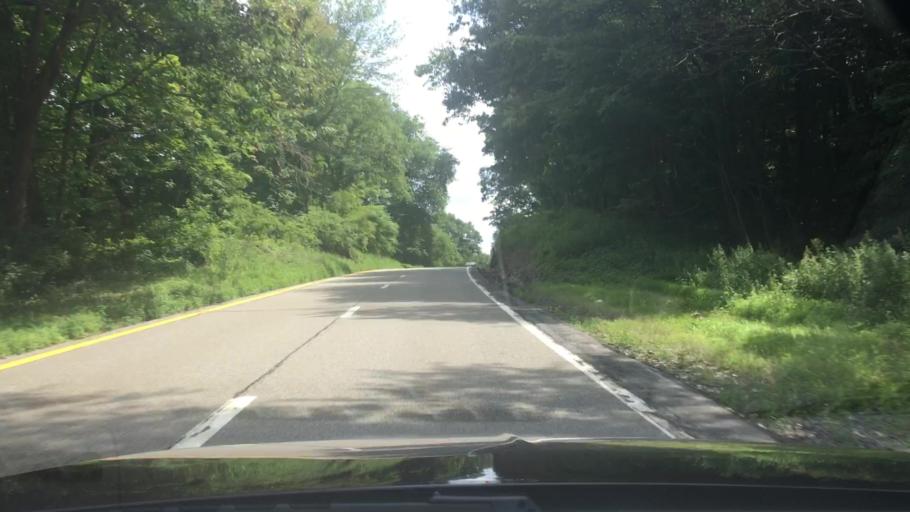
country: US
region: New York
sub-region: Dutchess County
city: Hillside Lake
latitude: 41.6216
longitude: -73.7682
